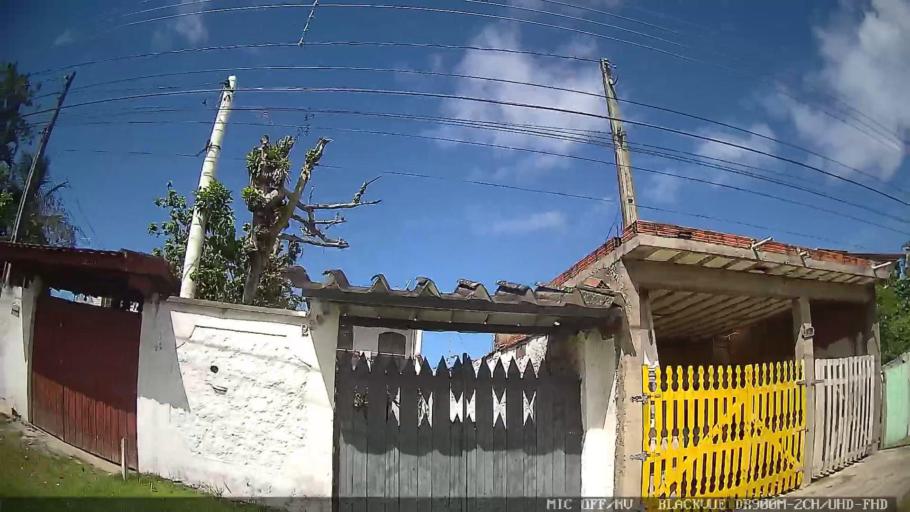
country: BR
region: Sao Paulo
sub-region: Itanhaem
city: Itanhaem
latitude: -24.2334
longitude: -46.8928
